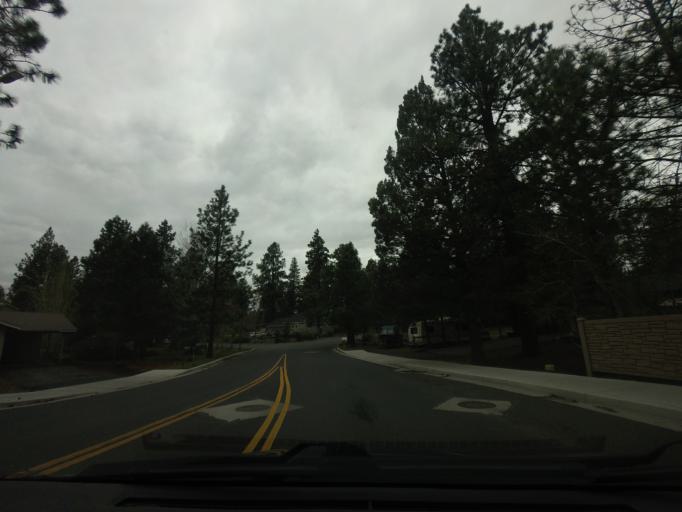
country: US
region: Oregon
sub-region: Deschutes County
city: Bend
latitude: 44.0217
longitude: -121.3287
